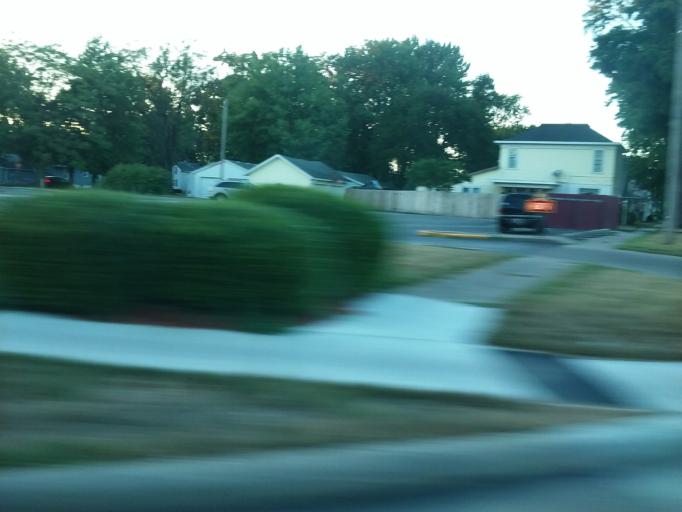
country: US
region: Ohio
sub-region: Hancock County
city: Findlay
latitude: 41.0458
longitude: -83.6405
